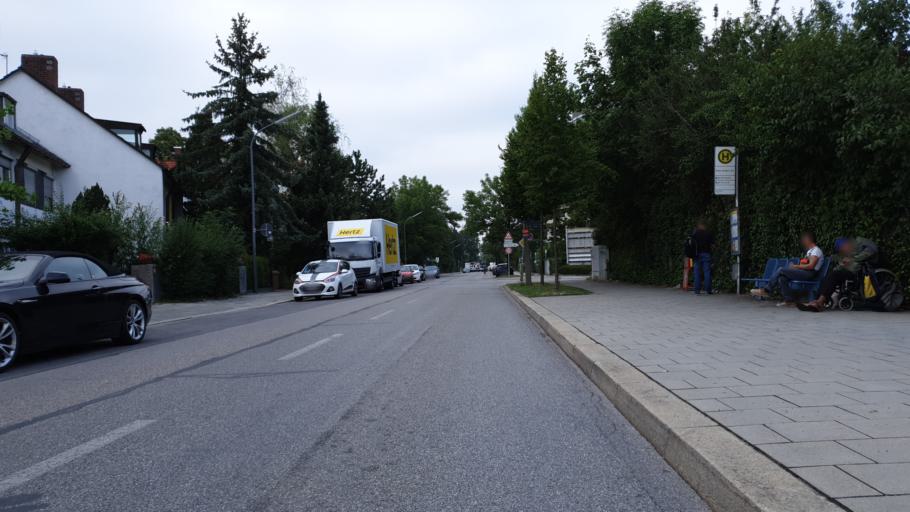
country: DE
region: Bavaria
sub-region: Upper Bavaria
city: Pasing
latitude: 48.1527
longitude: 11.4763
